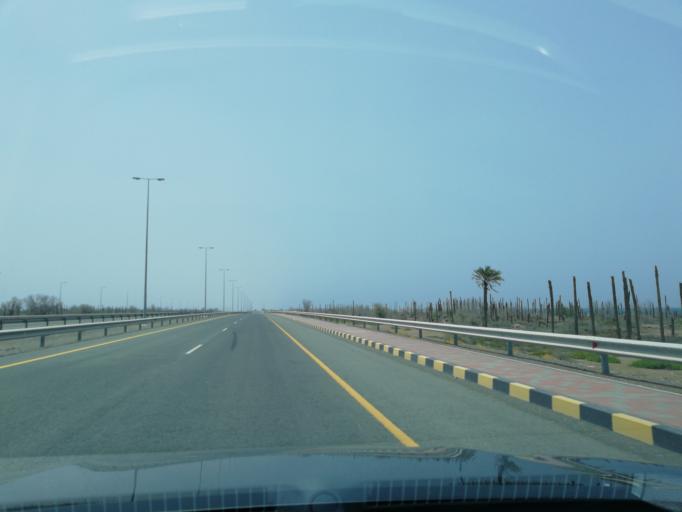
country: OM
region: Al Batinah
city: Shinas
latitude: 24.6479
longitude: 56.5168
